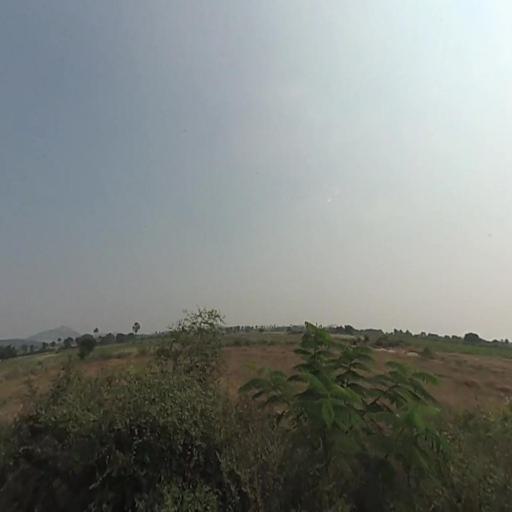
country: IN
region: Telangana
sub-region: Nalgonda
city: Nalgonda
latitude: 17.2031
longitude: 79.1445
